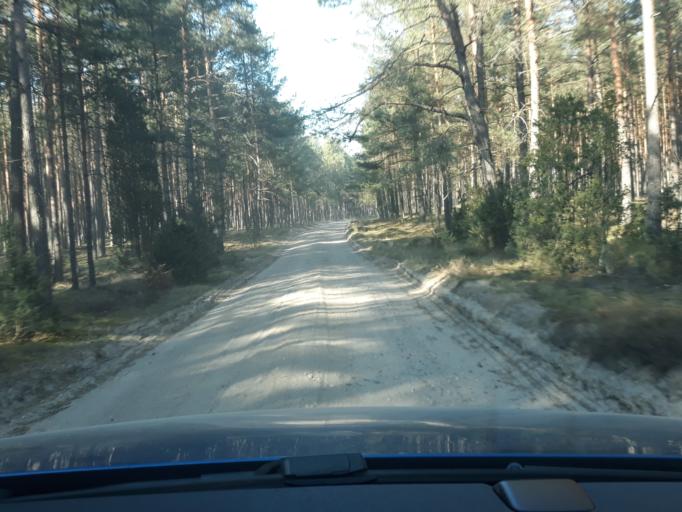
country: PL
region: Pomeranian Voivodeship
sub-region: Powiat bytowski
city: Lipnica
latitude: 53.9202
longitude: 17.4409
